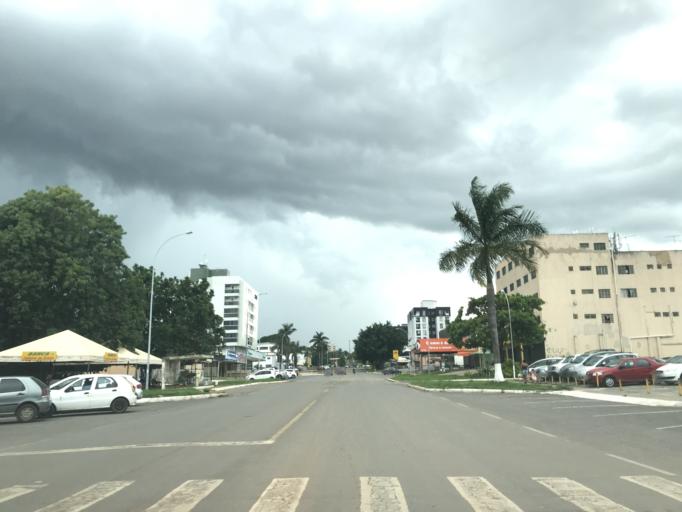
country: BR
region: Federal District
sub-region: Brasilia
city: Brasilia
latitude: -15.6470
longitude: -47.8060
